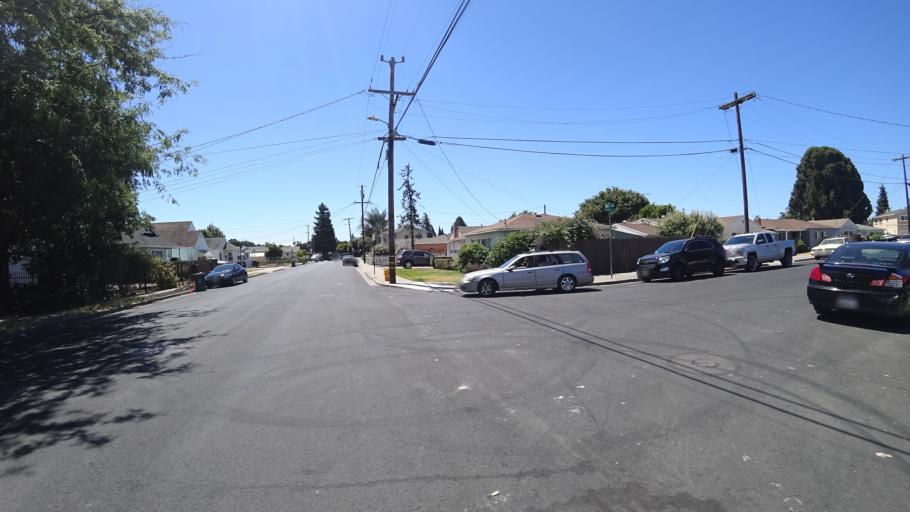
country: US
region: California
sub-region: Alameda County
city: Hayward
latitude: 37.6653
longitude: -122.0888
